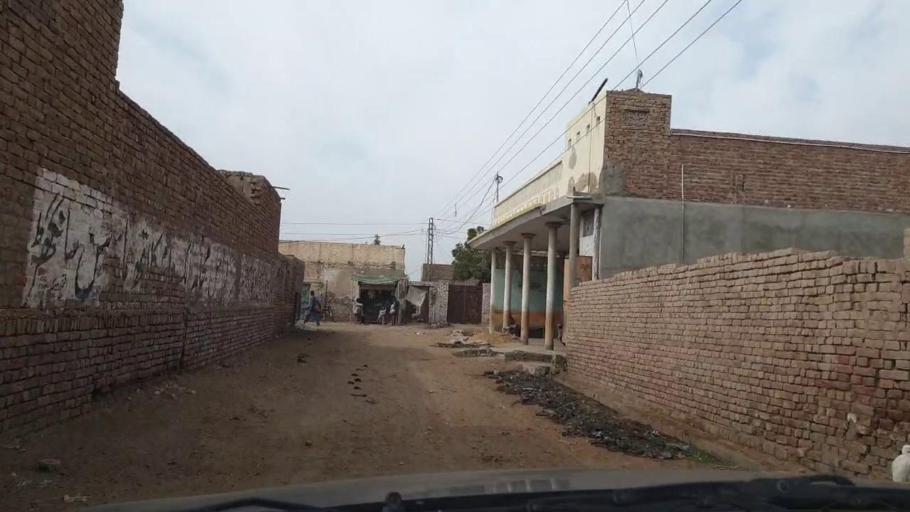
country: PK
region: Sindh
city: Sinjhoro
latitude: 26.0988
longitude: 68.8591
